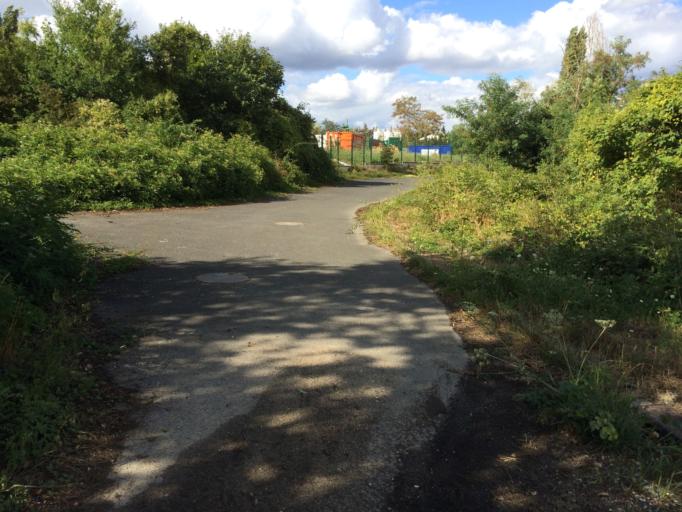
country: FR
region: Ile-de-France
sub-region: Departement de l'Essonne
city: Saulx-les-Chartreux
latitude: 48.6959
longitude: 2.2662
